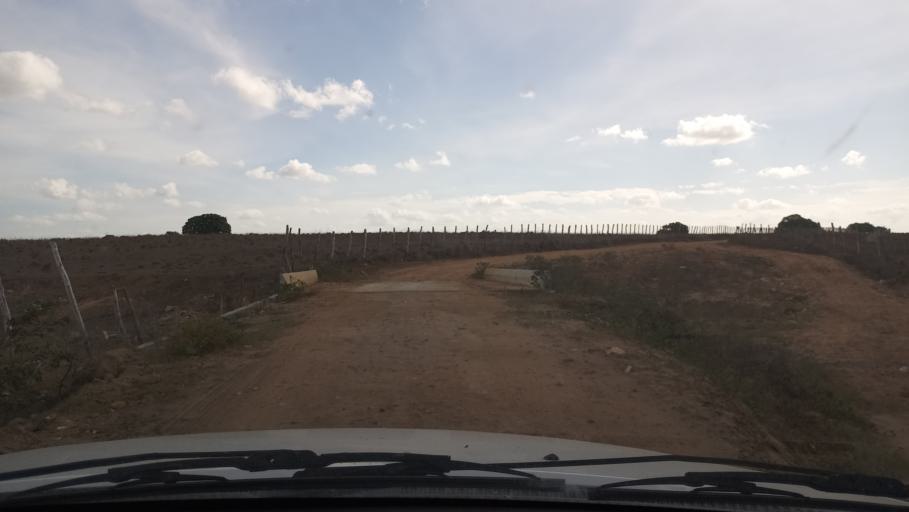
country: BR
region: Rio Grande do Norte
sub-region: Goianinha
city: Goianinha
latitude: -6.3034
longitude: -35.3019
